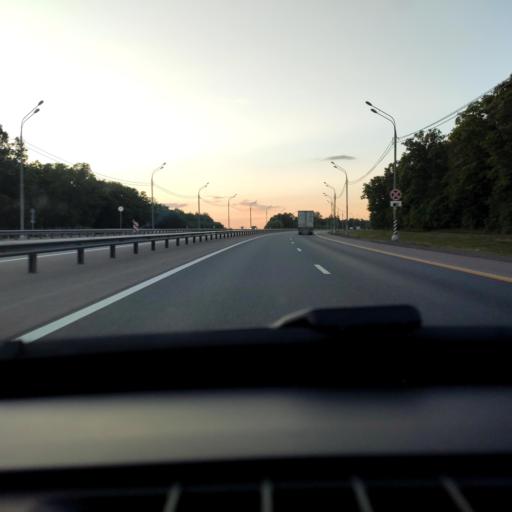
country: RU
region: Lipetsk
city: Khlevnoye
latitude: 52.2449
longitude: 39.0663
